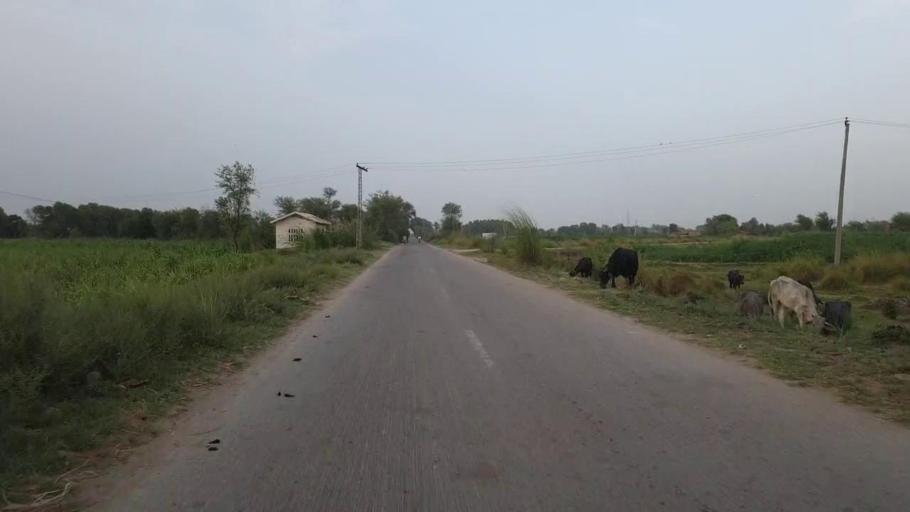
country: PK
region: Sindh
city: Daur
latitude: 26.4203
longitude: 68.2501
